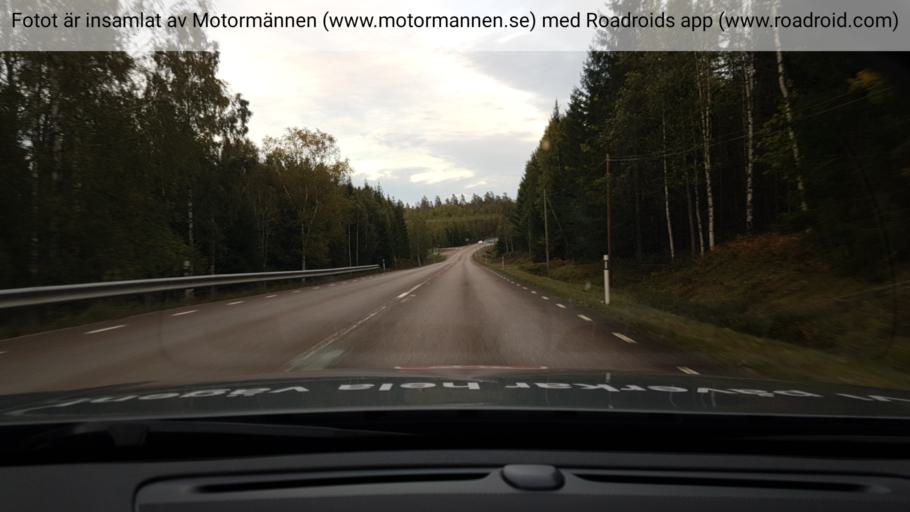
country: SE
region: Vaestra Goetaland
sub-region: Amals Kommun
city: Amal
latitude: 59.0801
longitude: 12.6090
